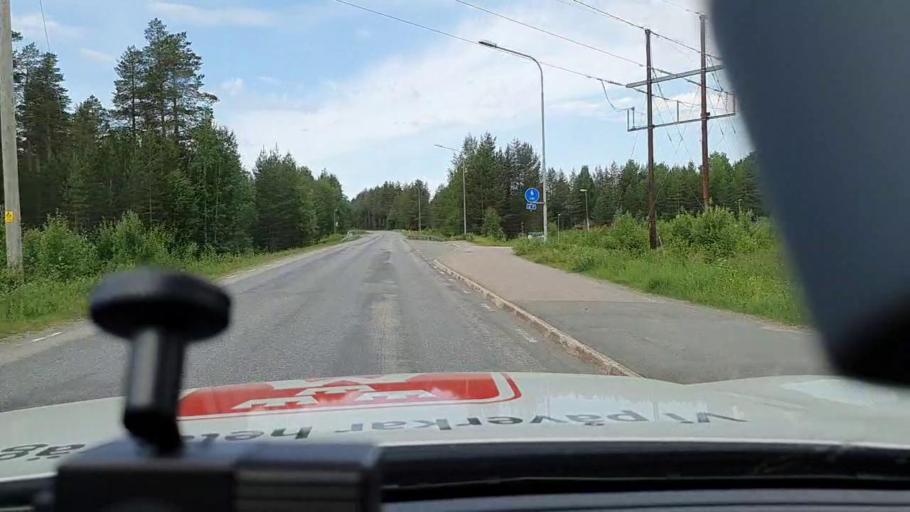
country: SE
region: Norrbotten
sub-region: Bodens Kommun
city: Boden
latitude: 65.8153
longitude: 21.6105
